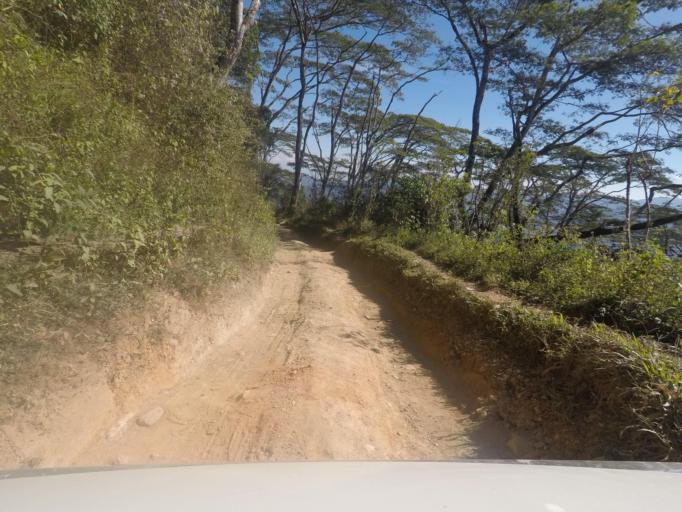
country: TL
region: Ermera
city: Gleno
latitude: -8.7321
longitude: 125.3416
